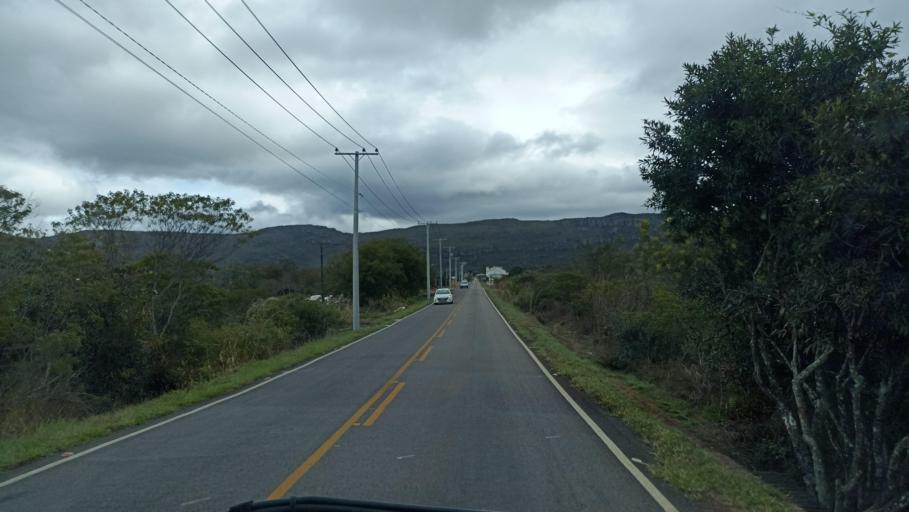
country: BR
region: Bahia
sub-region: Andarai
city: Vera Cruz
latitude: -12.9993
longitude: -41.3625
